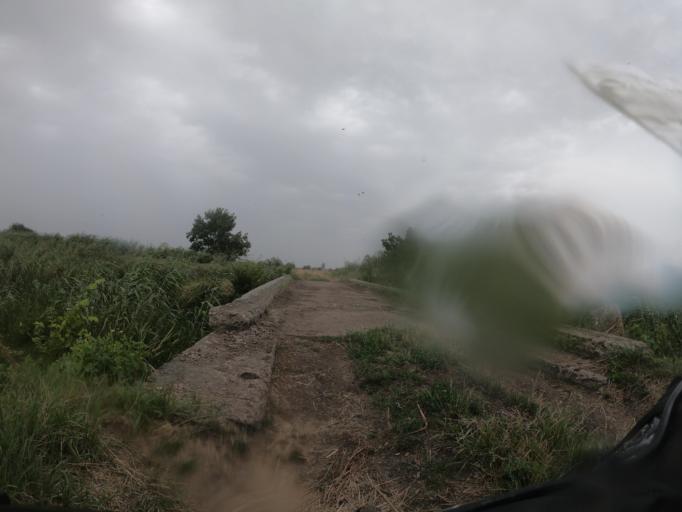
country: HU
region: Heves
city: Poroszlo
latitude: 47.7008
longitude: 20.5922
